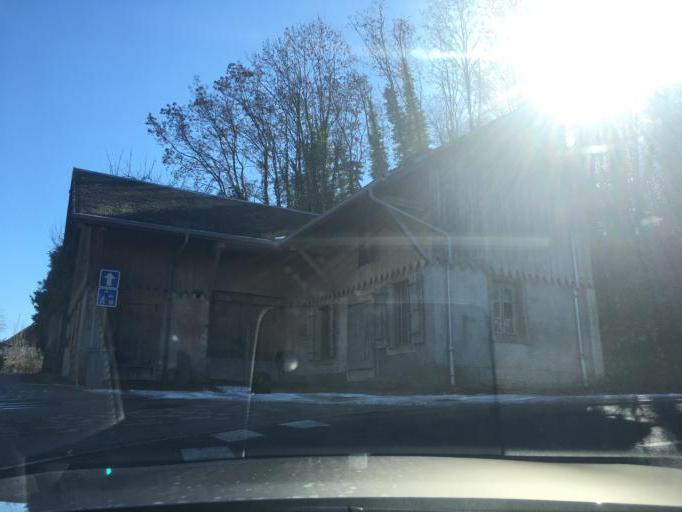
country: FR
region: Rhone-Alpes
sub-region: Departement de la Haute-Savoie
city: Vetraz-Monthoux
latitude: 46.1866
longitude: 6.2596
